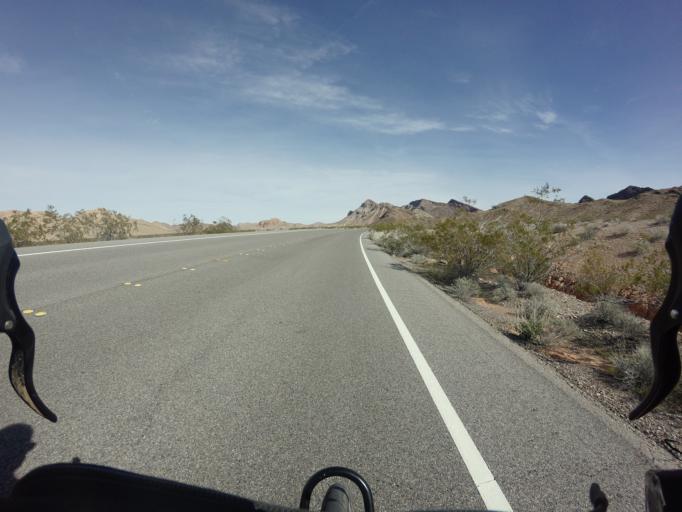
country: US
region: Nevada
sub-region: Clark County
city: Boulder City
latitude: 36.2068
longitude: -114.6652
